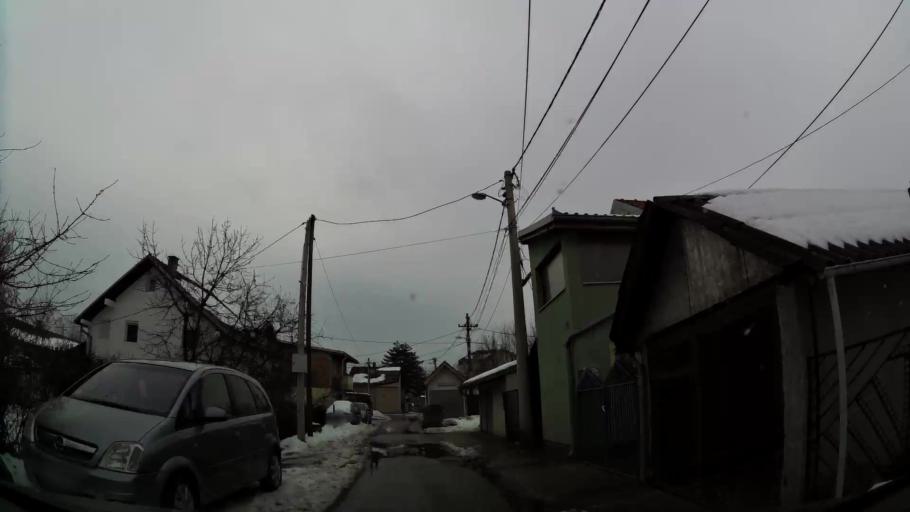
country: RS
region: Central Serbia
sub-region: Belgrade
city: Zemun
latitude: 44.8339
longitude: 20.3763
